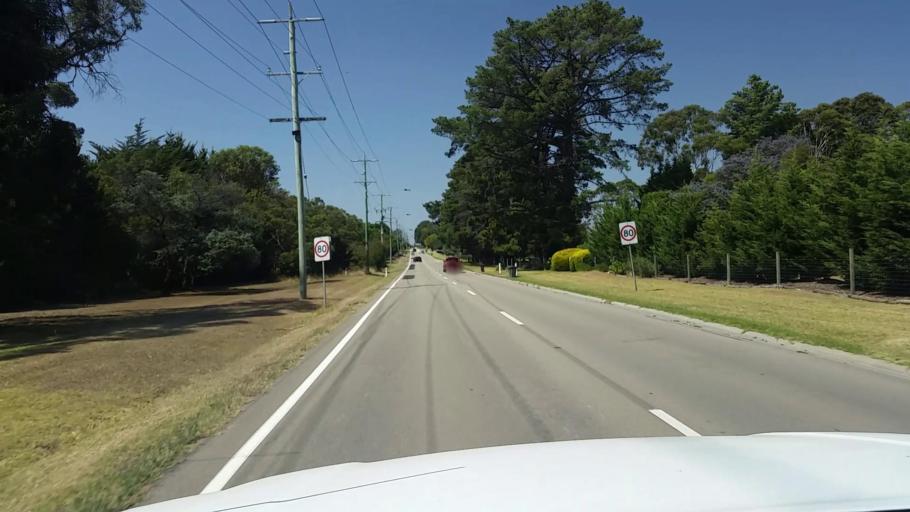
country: AU
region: Victoria
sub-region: Mornington Peninsula
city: Somerville
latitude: -38.2368
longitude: 145.1610
